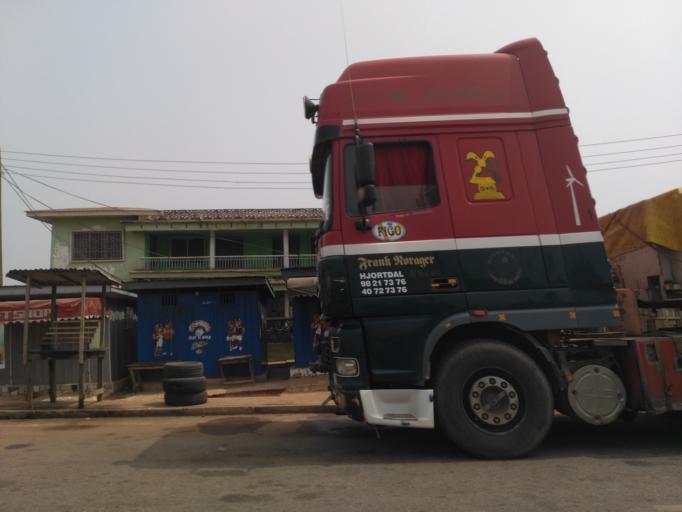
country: GH
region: Ashanti
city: Kumasi
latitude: 6.6969
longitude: -1.6460
